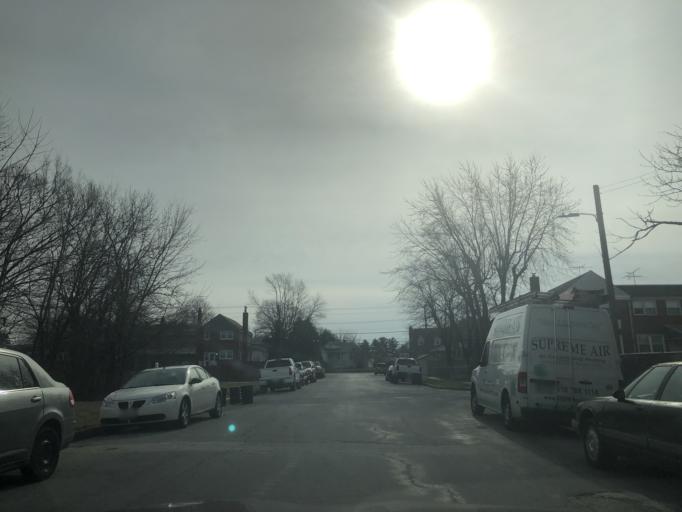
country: US
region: Maryland
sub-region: Baltimore County
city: Dundalk
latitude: 39.2730
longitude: -76.4971
